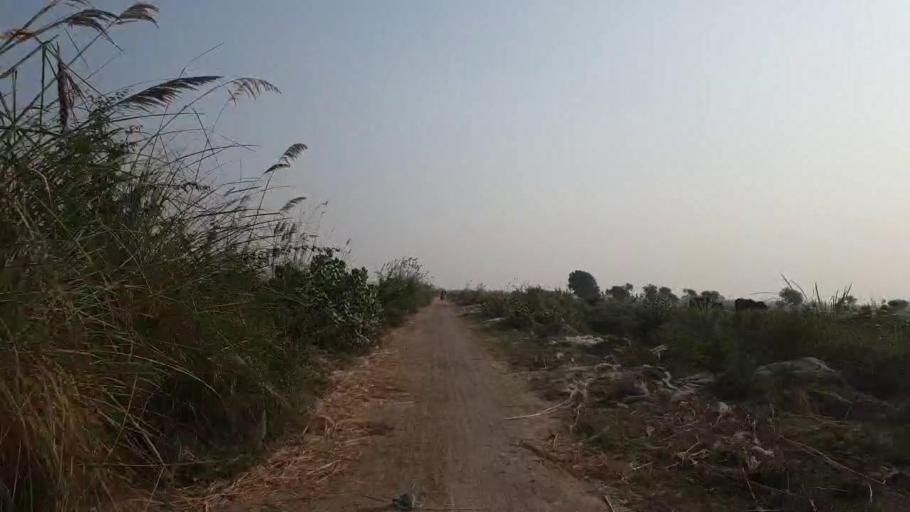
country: PK
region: Sindh
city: Tando Muhammad Khan
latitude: 25.0992
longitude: 68.3543
